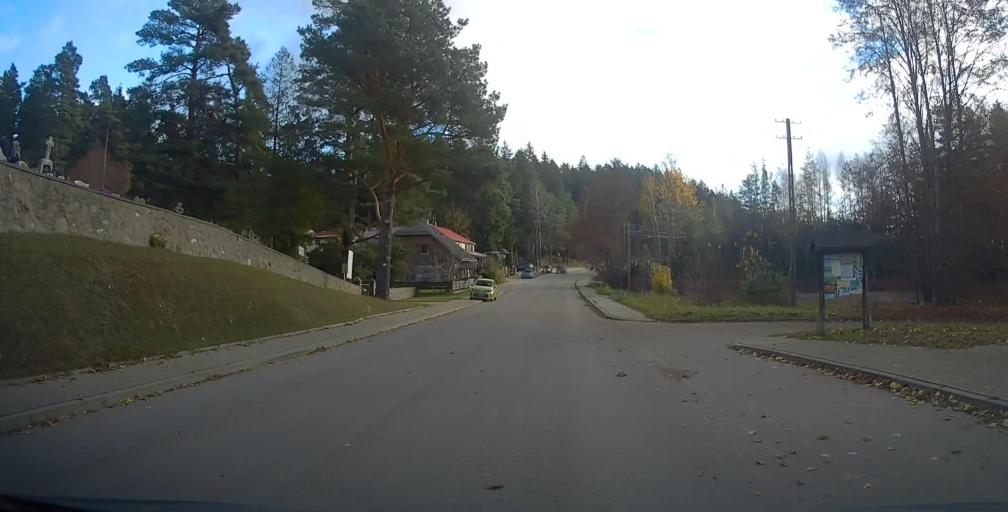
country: PL
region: Podlasie
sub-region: Suwalki
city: Suwalki
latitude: 54.2872
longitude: 22.8866
